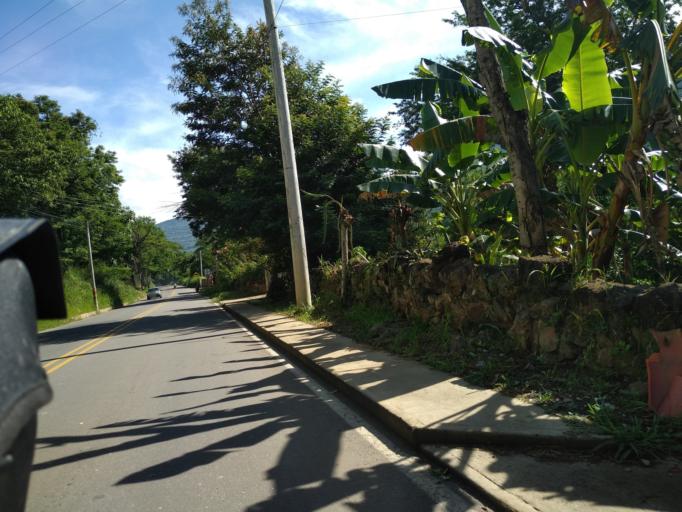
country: CO
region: Santander
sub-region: San Gil
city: San Gil
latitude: 6.5319
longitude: -73.1255
